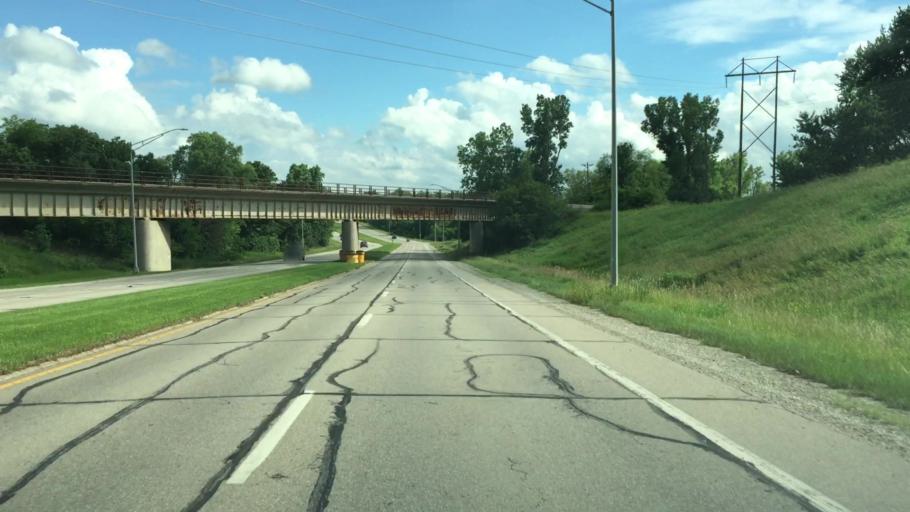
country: US
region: Iowa
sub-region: Jasper County
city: Newton
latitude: 41.6958
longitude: -93.0766
